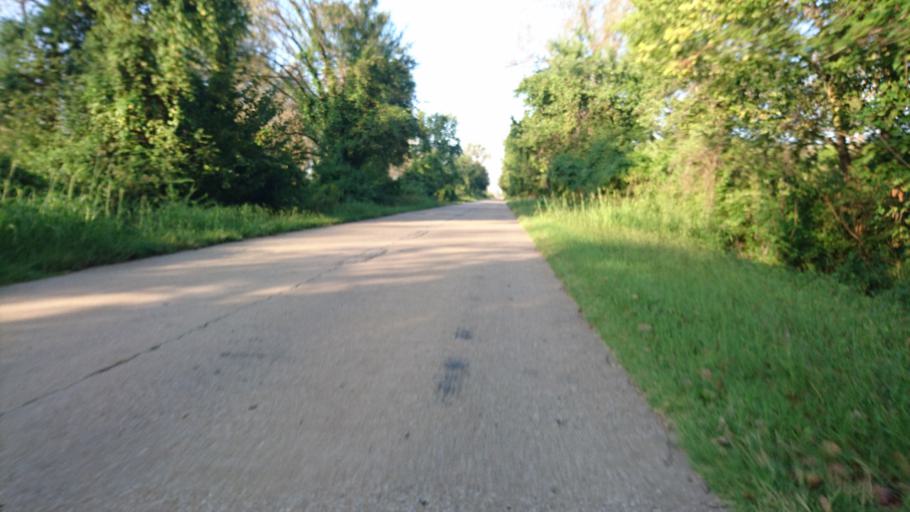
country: US
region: Missouri
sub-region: Saint Louis County
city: Glasgow Village
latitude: 38.7608
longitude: -90.1469
